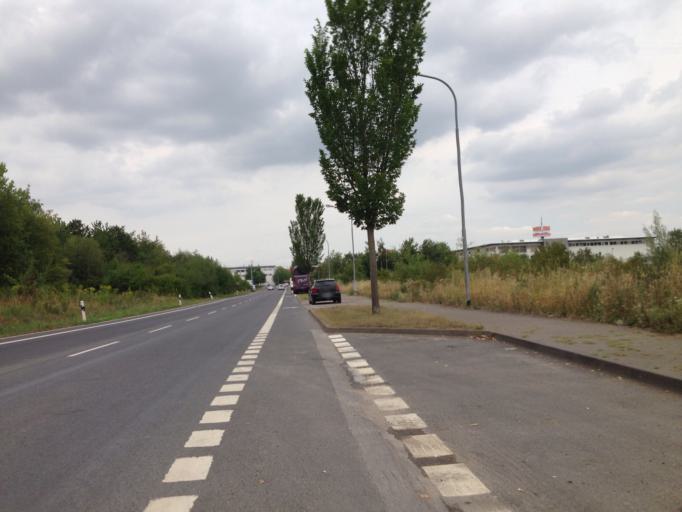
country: DE
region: Hesse
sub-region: Regierungsbezirk Giessen
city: Giessen
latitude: 50.5672
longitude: 8.6921
